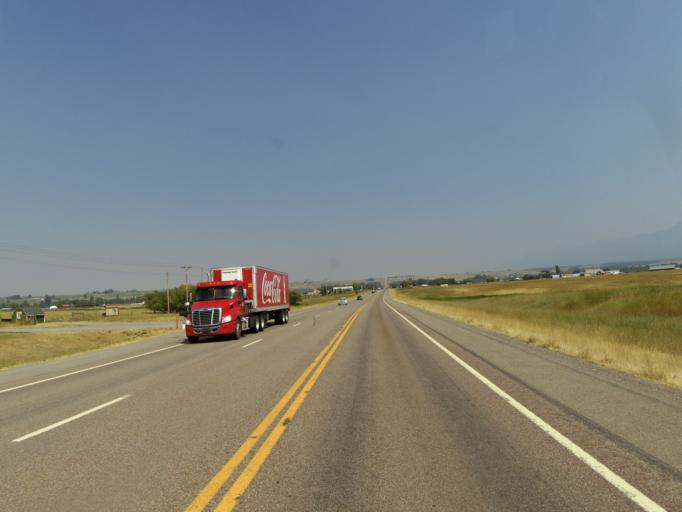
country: US
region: Montana
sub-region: Lake County
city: Ronan
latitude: 47.3778
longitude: -114.0968
